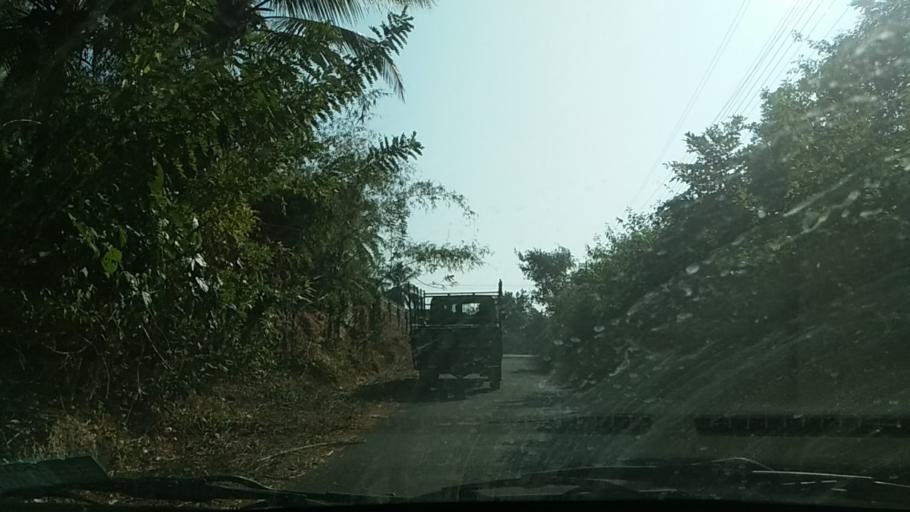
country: IN
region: Goa
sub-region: North Goa
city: Ponda
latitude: 15.4007
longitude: 74.0617
